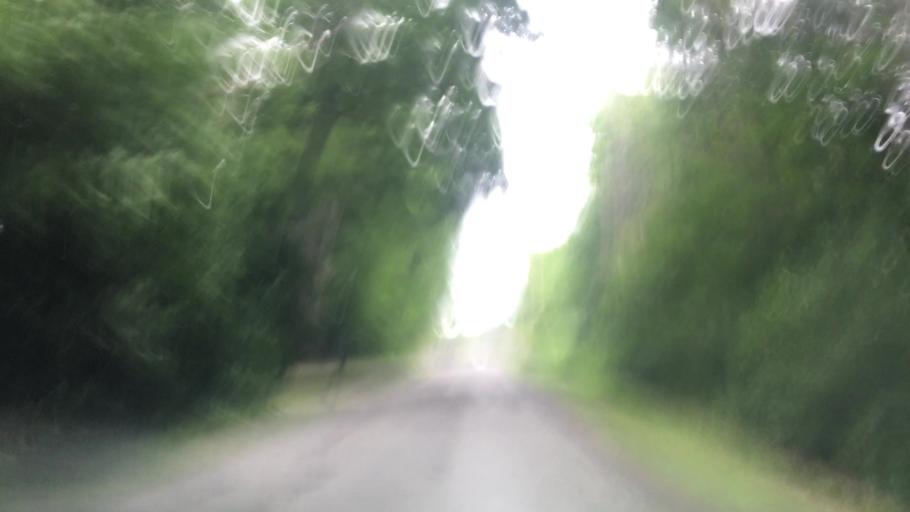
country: US
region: Maine
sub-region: Penobscot County
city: Veazie
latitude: 44.8481
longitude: -68.7466
